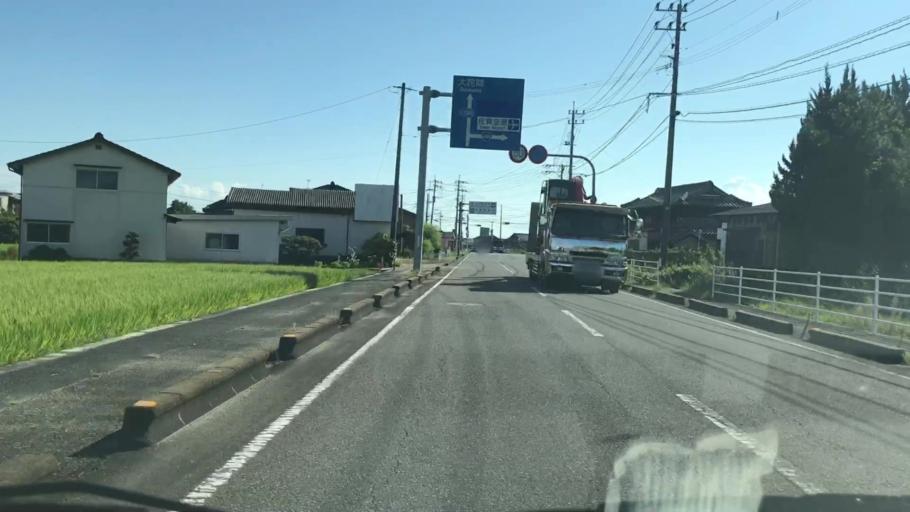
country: JP
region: Saga Prefecture
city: Okawa
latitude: 33.1919
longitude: 130.3324
